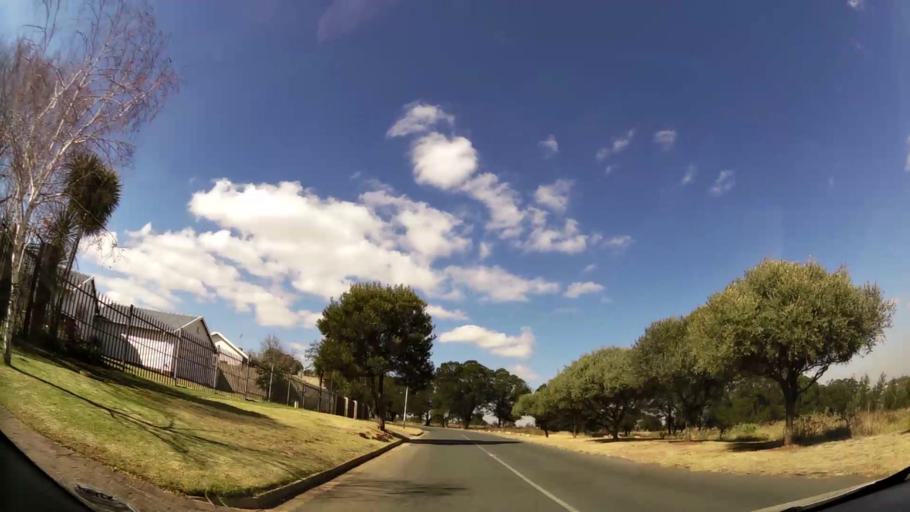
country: ZA
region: Gauteng
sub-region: West Rand District Municipality
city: Krugersdorp
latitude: -26.1072
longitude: 27.7994
